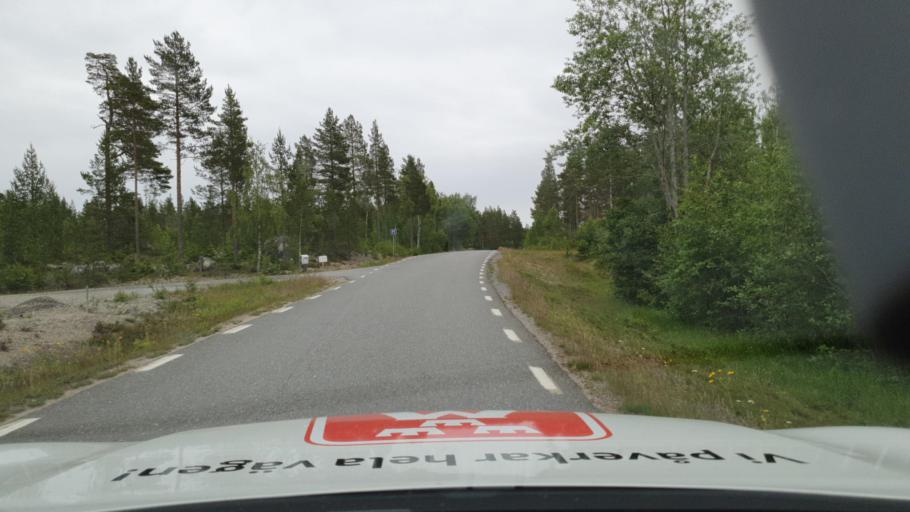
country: SE
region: Vaesterbotten
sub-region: Nordmalings Kommun
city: Nordmaling
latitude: 63.4325
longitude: 19.4868
